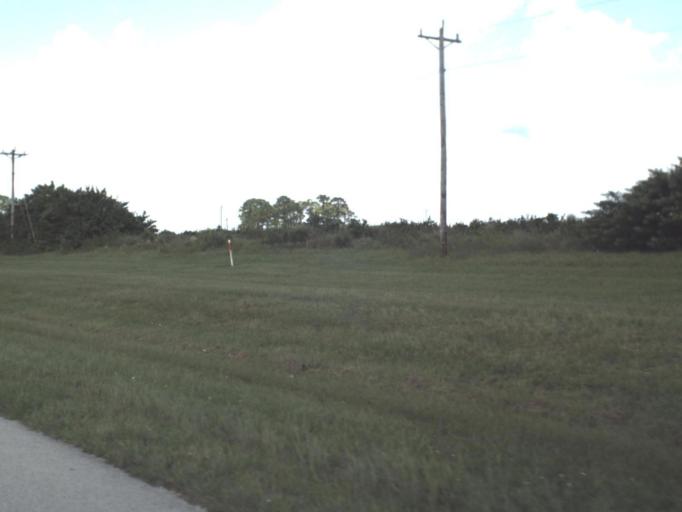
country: US
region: Florida
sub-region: Collier County
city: Immokalee
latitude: 26.4987
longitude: -81.4862
